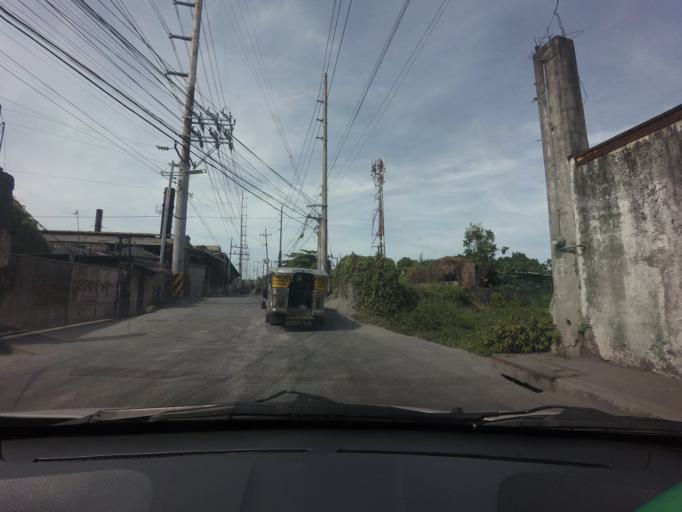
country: PH
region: Calabarzon
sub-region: Province of Rizal
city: Pateros
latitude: 14.5441
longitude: 121.0887
